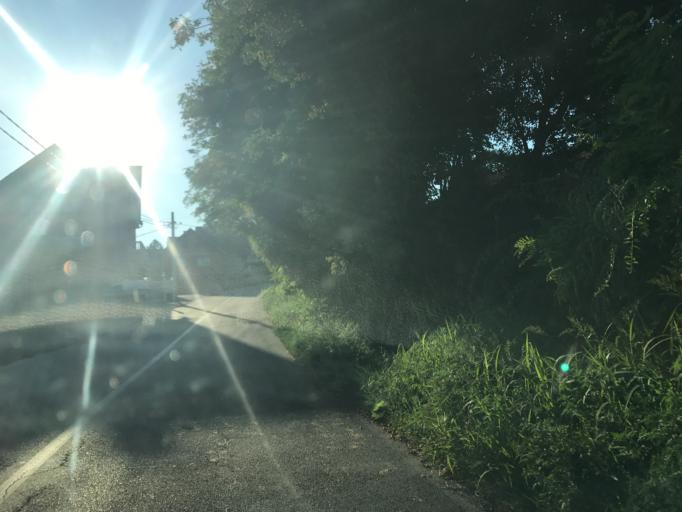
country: RO
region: Mehedinti
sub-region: Comuna Gogosu
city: Ostrovu Mare
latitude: 44.2900
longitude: 22.3544
